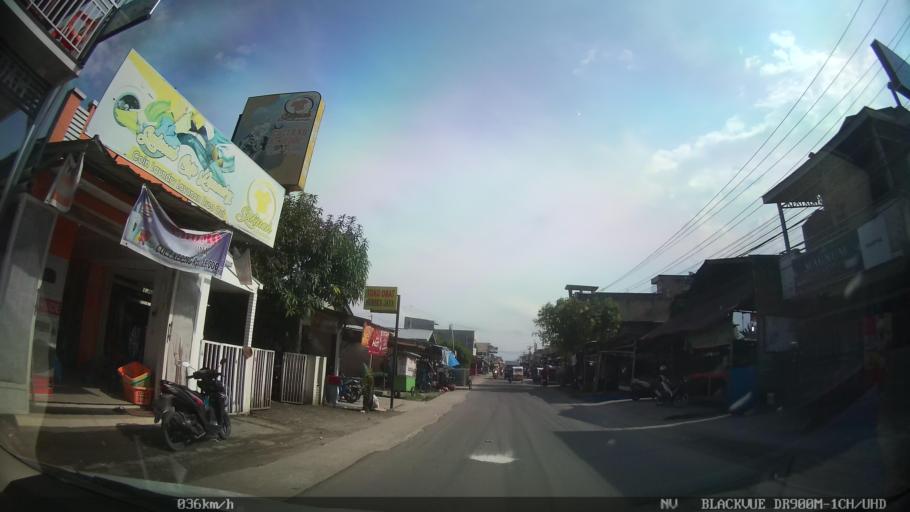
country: ID
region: North Sumatra
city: Medan
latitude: 3.5897
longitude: 98.7570
